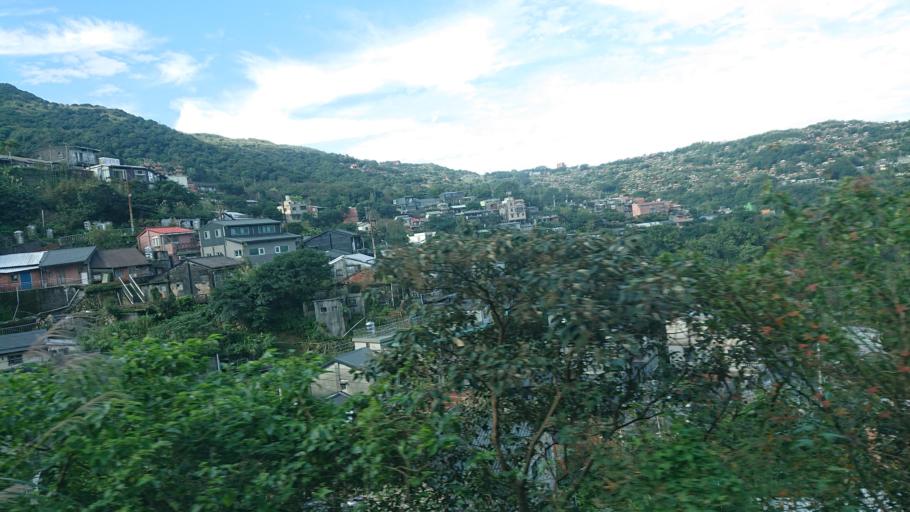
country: TW
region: Taiwan
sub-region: Keelung
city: Keelung
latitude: 25.1078
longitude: 121.8564
